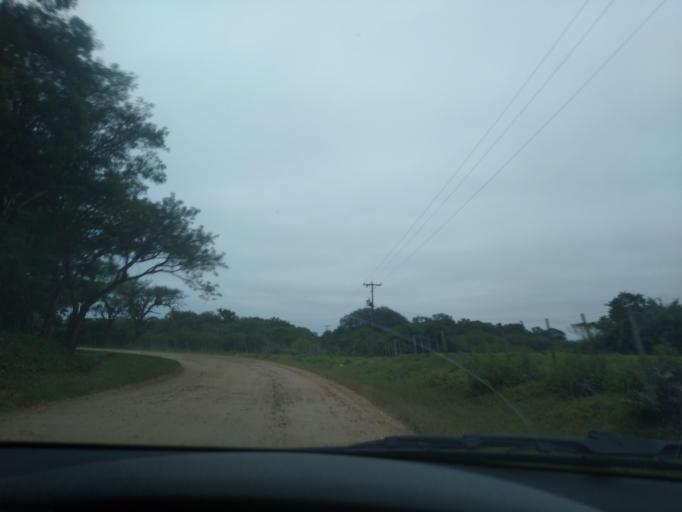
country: AR
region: Chaco
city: Colonia Benitez
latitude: -27.3480
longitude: -58.9707
